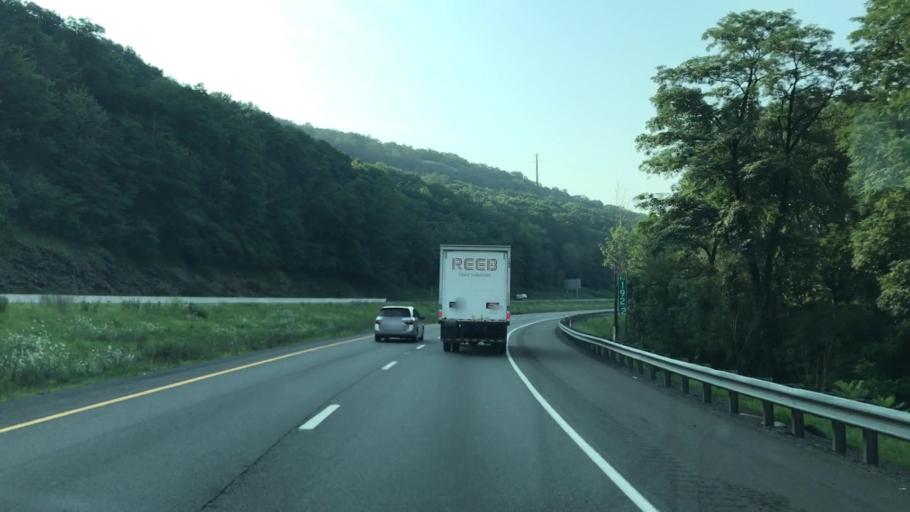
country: US
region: Pennsylvania
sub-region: Lackawanna County
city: Chinchilla
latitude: 41.4674
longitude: -75.6680
